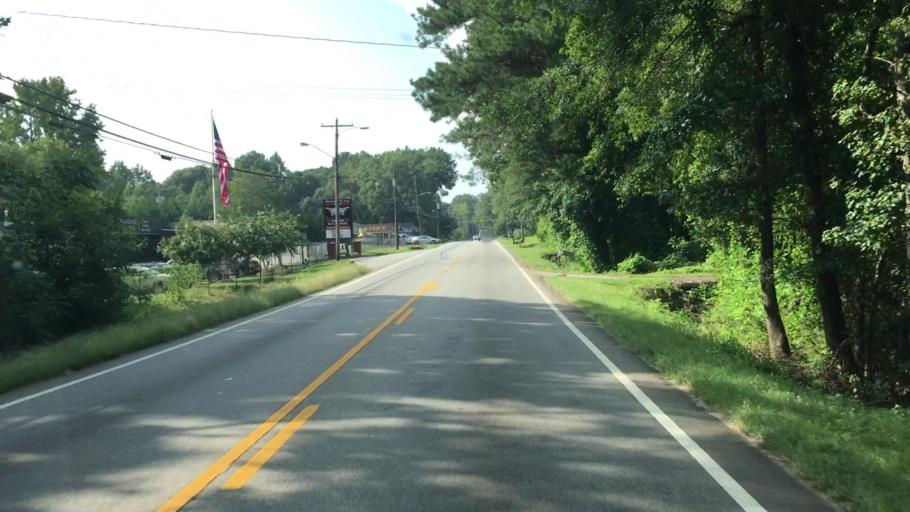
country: US
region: Georgia
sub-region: Walton County
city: Monroe
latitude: 33.7773
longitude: -83.7053
